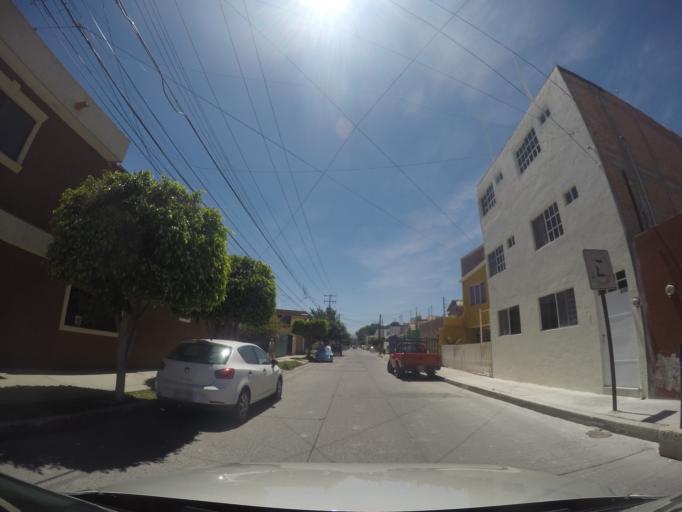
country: MX
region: San Luis Potosi
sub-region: San Luis Potosi
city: San Luis Potosi
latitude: 22.1584
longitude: -100.9903
